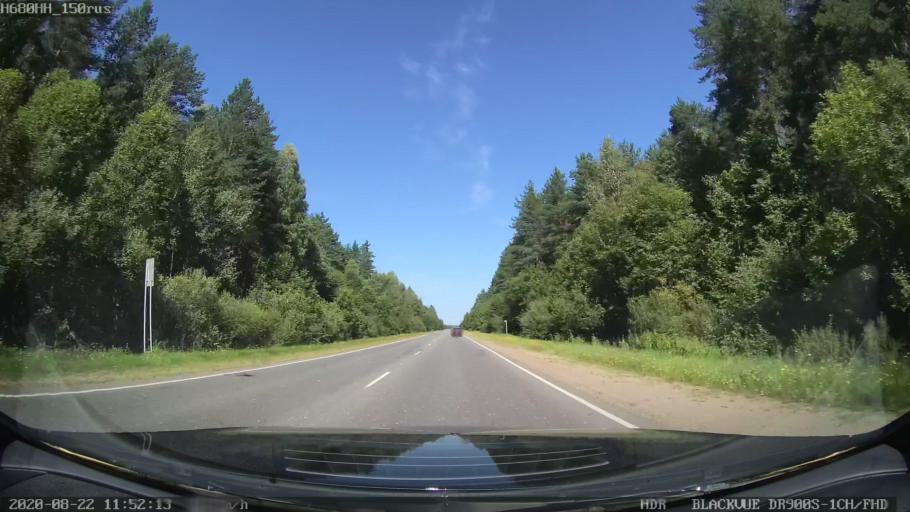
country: RU
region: Tverskaya
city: Vasil'yevskiy Mokh
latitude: 57.1125
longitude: 36.1184
